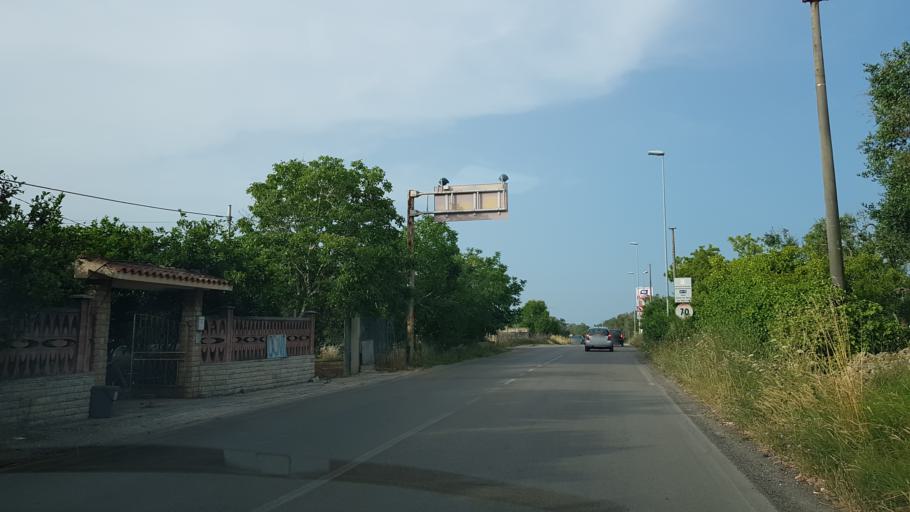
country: IT
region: Apulia
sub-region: Provincia di Brindisi
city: Cellino San Marco
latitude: 40.4785
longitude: 17.9799
